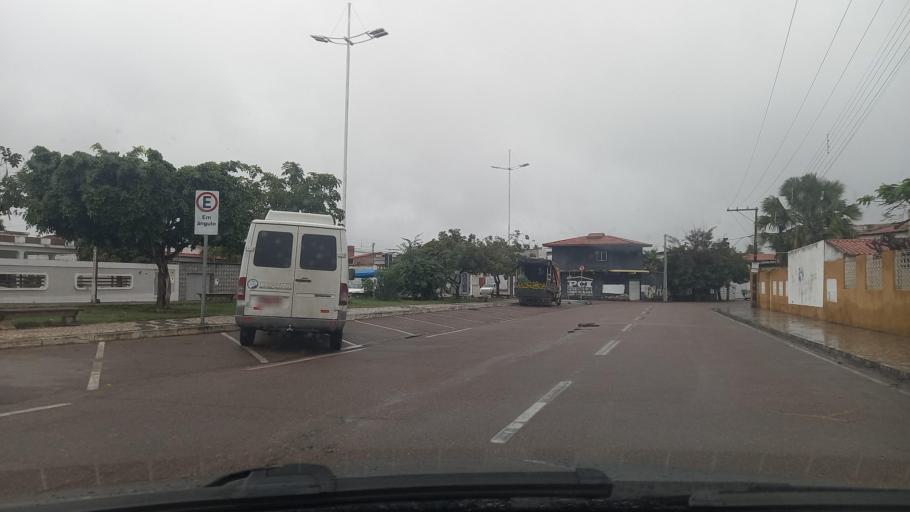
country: BR
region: Bahia
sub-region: Paulo Afonso
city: Paulo Afonso
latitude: -9.4055
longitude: -38.2254
